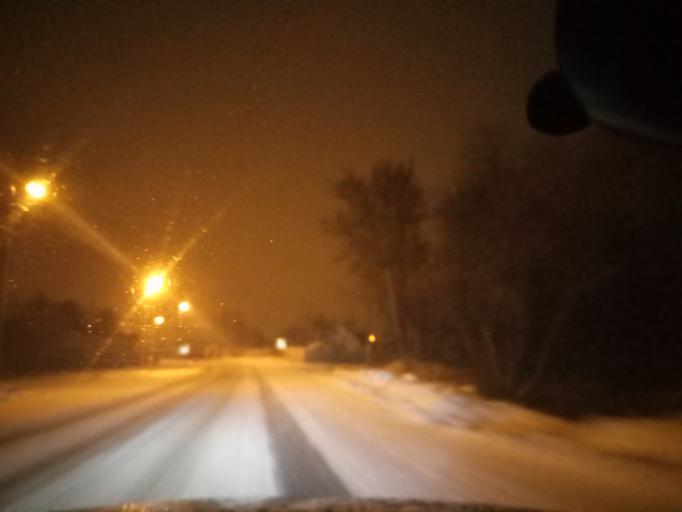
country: RU
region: Tula
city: Novomoskovsk
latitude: 53.9983
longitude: 38.2957
